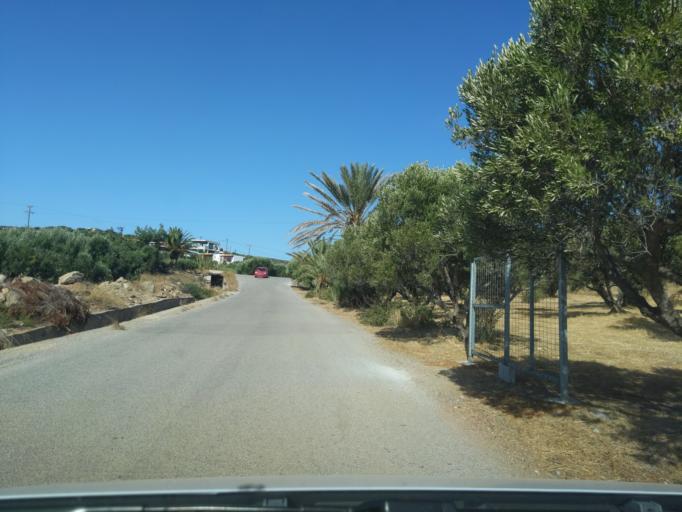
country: GR
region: Crete
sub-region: Nomos Lasithiou
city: Palekastro
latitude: 35.2159
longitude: 26.2655
